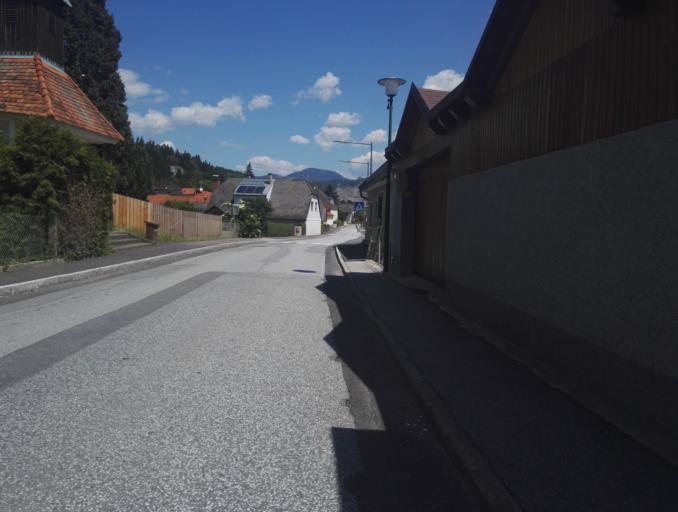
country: AT
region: Styria
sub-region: Politischer Bezirk Graz-Umgebung
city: Deutschfeistritz
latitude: 47.1797
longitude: 15.3232
